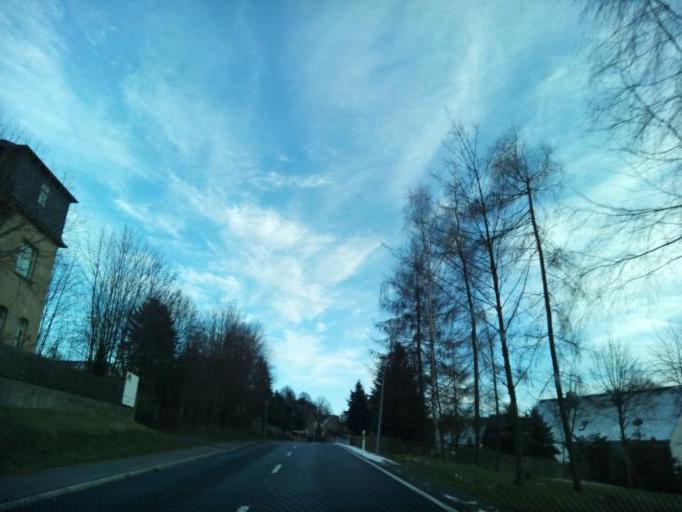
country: DE
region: Saxony
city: Bornichen
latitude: 50.7664
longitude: 13.1190
